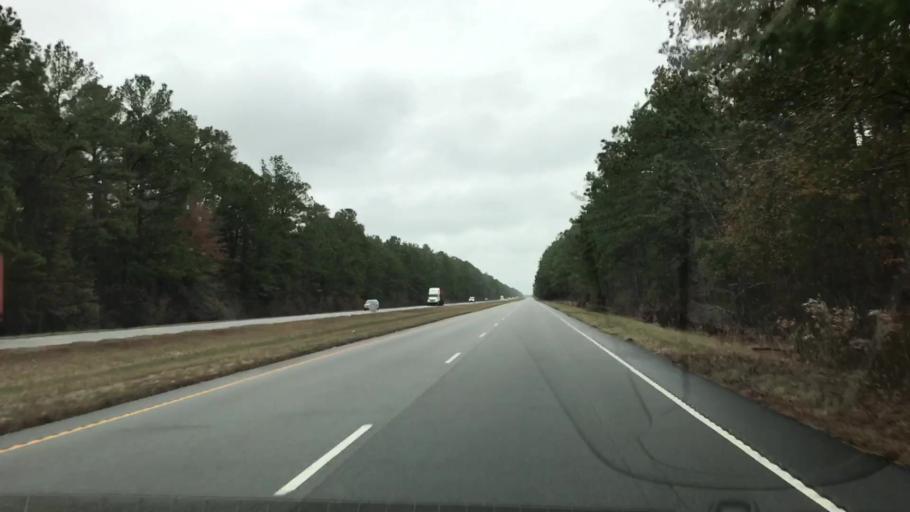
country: US
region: South Carolina
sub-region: Charleston County
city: Awendaw
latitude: 33.1427
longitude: -79.4382
